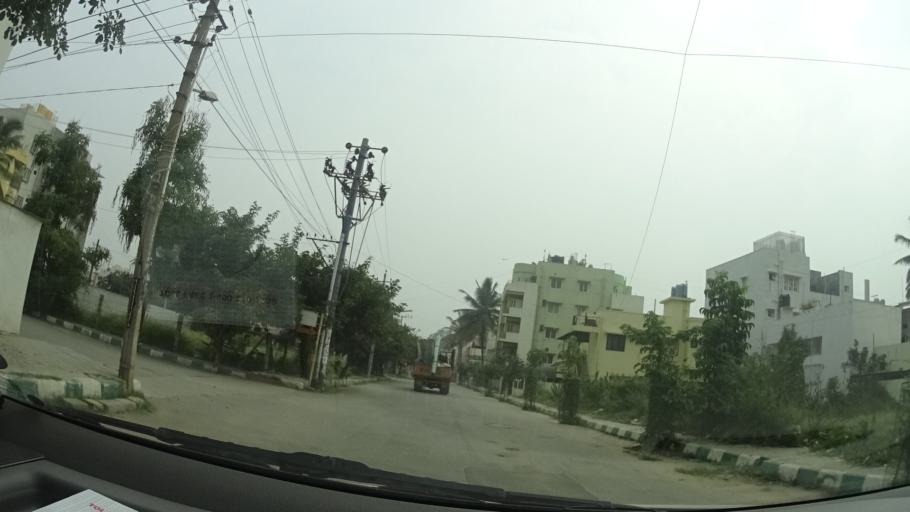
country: IN
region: Karnataka
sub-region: Bangalore Urban
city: Yelahanka
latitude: 13.0401
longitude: 77.6270
